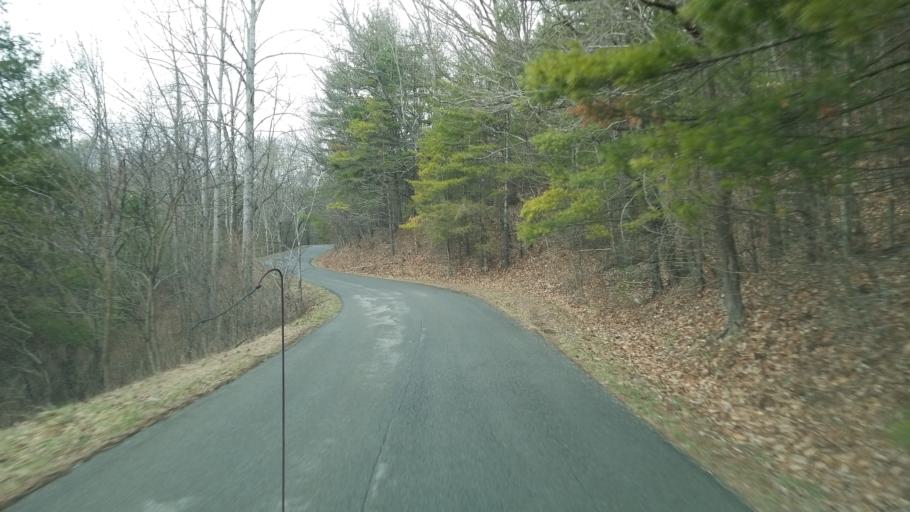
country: US
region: Virginia
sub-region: Giles County
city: Pearisburg
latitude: 37.2202
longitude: -80.7005
